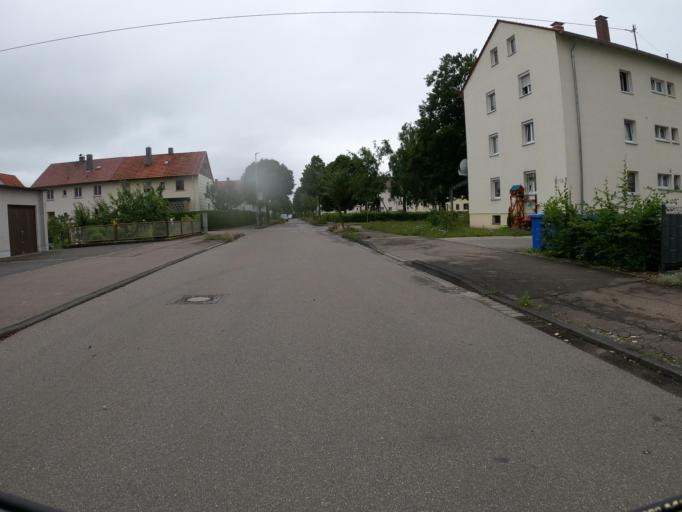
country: DE
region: Baden-Wuerttemberg
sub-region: Tuebingen Region
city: Langenau
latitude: 48.4903
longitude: 10.1147
